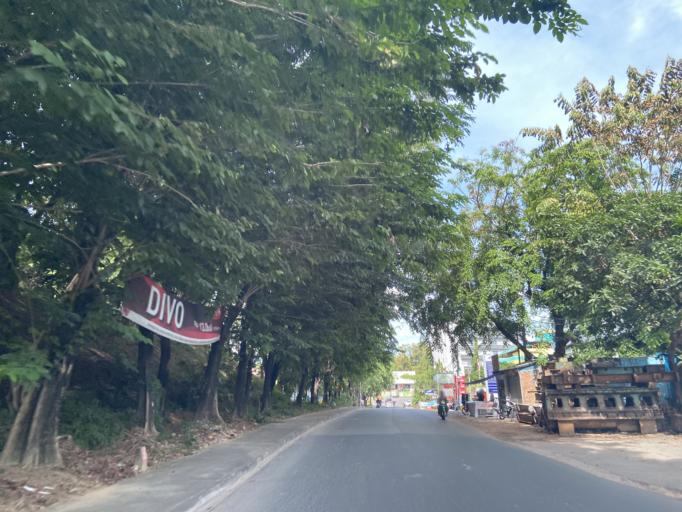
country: SG
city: Singapore
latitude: 1.1484
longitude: 104.0178
